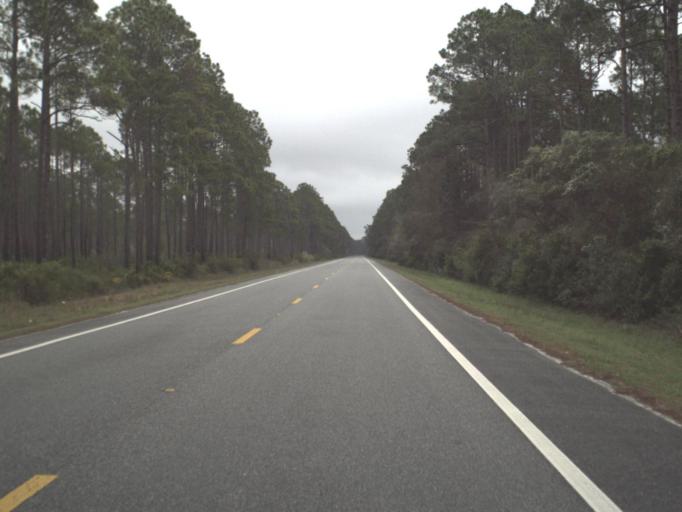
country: US
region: Florida
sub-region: Franklin County
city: Eastpoint
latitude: 29.8290
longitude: -84.8752
